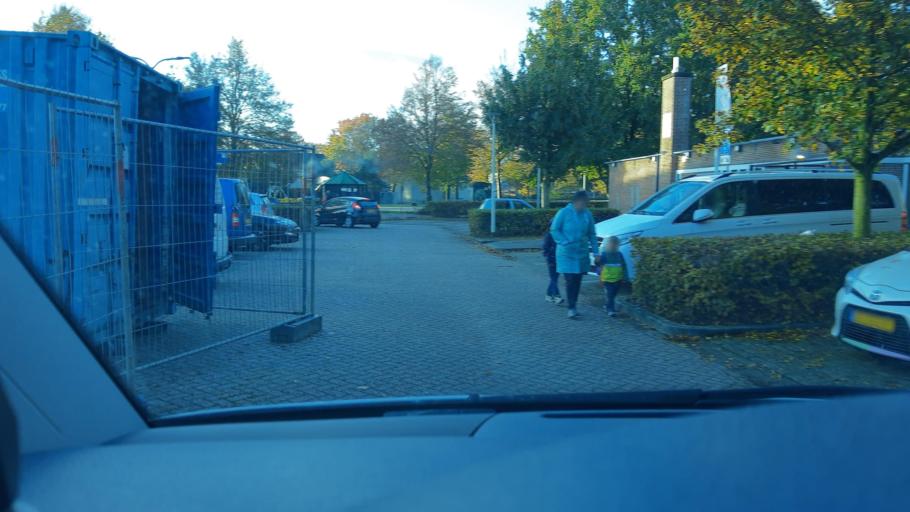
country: NL
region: Gelderland
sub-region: Gemeente Nijmegen
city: Lindenholt
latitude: 51.8318
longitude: 5.8007
